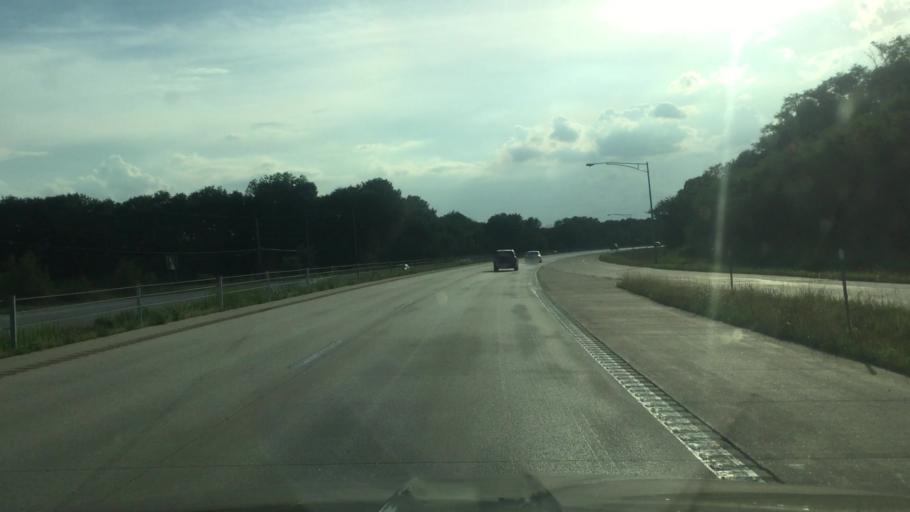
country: US
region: Missouri
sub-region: Jackson County
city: Lone Jack
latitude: 38.8683
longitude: -94.1757
